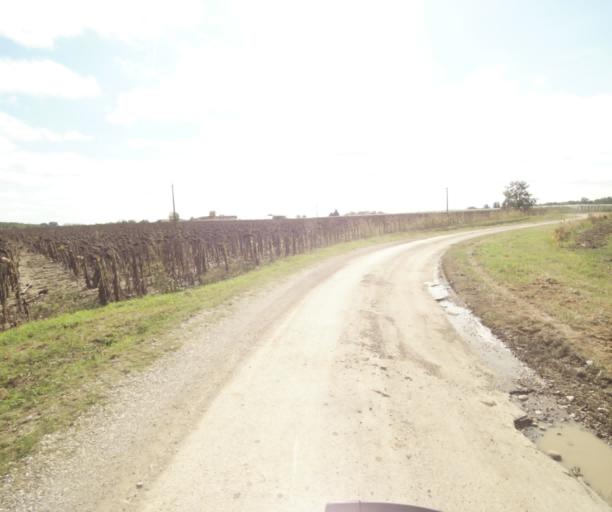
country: FR
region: Midi-Pyrenees
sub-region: Departement du Tarn-et-Garonne
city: Montech
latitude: 43.9452
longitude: 1.2067
